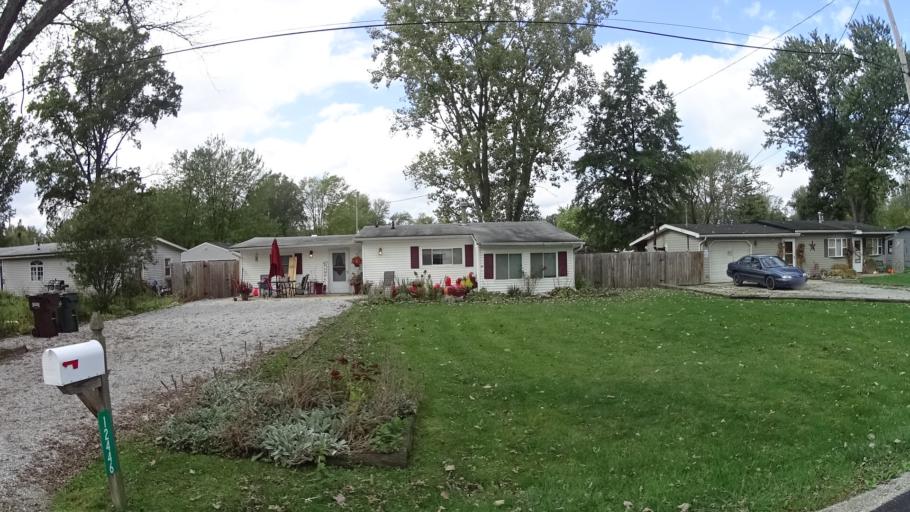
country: US
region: Ohio
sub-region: Lorain County
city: Eaton Estates
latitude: 41.3077
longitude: -82.0029
